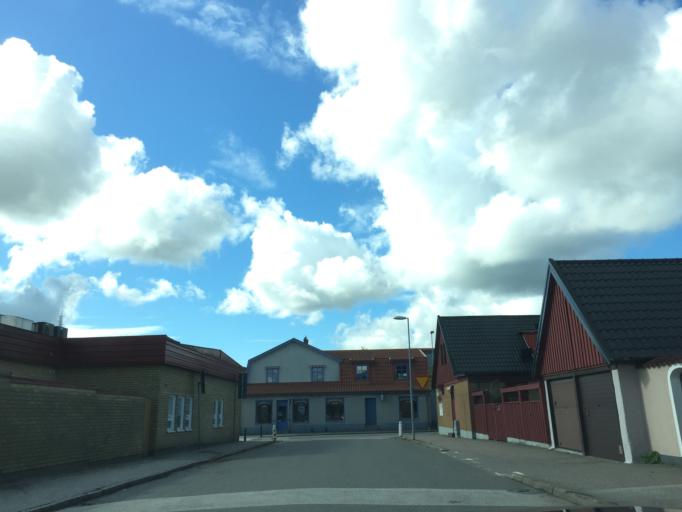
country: SE
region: Skane
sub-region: Sjobo Kommun
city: Sjoebo
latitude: 55.6331
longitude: 13.7071
